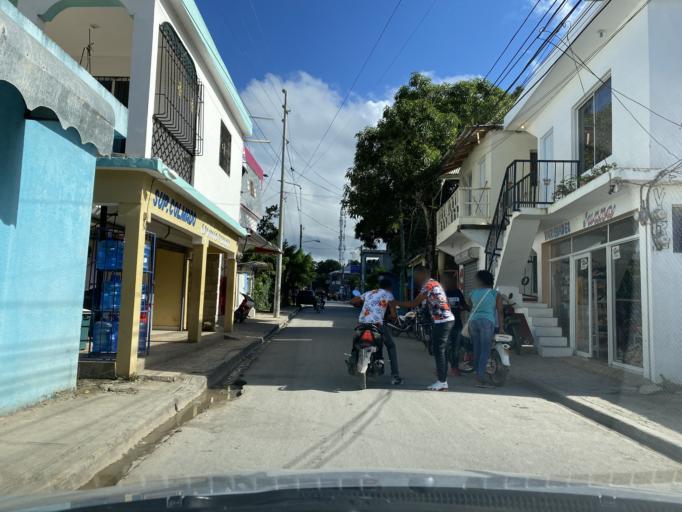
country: DO
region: Samana
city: Las Terrenas
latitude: 19.3082
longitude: -69.5450
